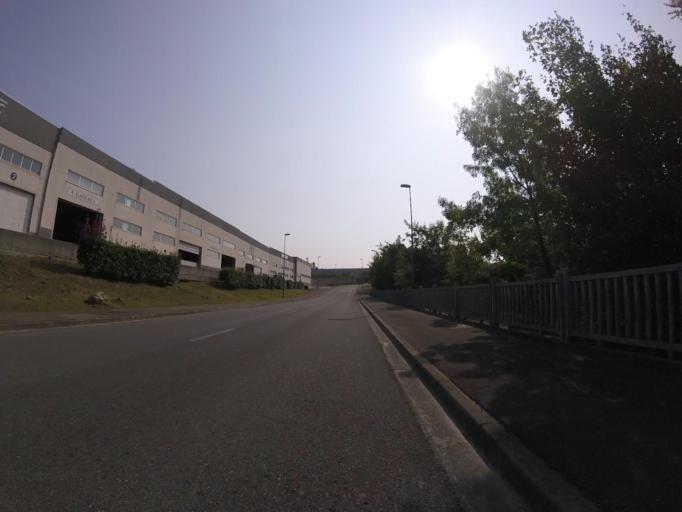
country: ES
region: Basque Country
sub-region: Provincia de Guipuzcoa
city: Errenteria
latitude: 43.2963
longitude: -1.8977
